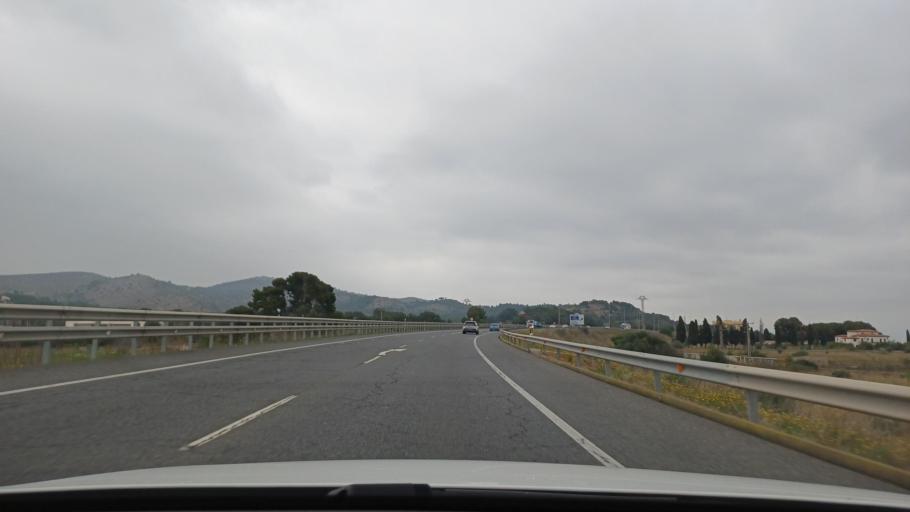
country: ES
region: Valencia
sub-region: Provincia de Castello
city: Borriol
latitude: 40.0003
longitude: -0.0859
